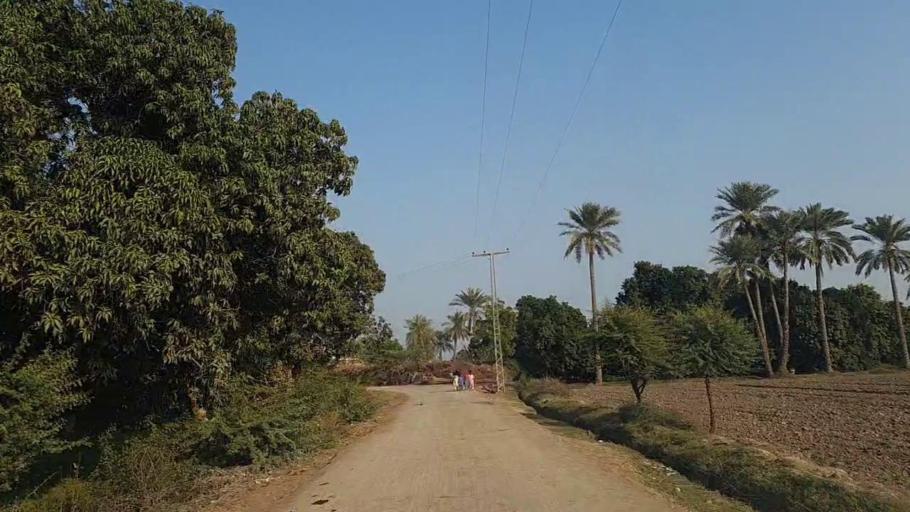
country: PK
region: Sindh
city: Jam Sahib
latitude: 26.2304
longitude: 68.5990
